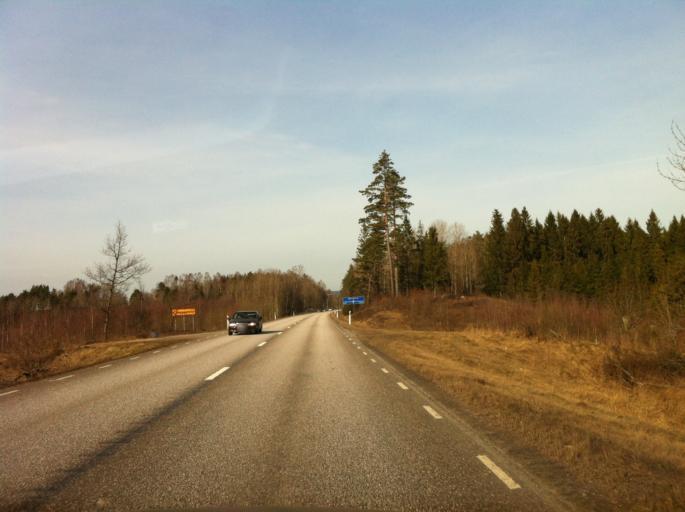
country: SE
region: Vaestra Goetaland
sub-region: Skovde Kommun
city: Skultorp
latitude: 58.2488
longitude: 13.8156
